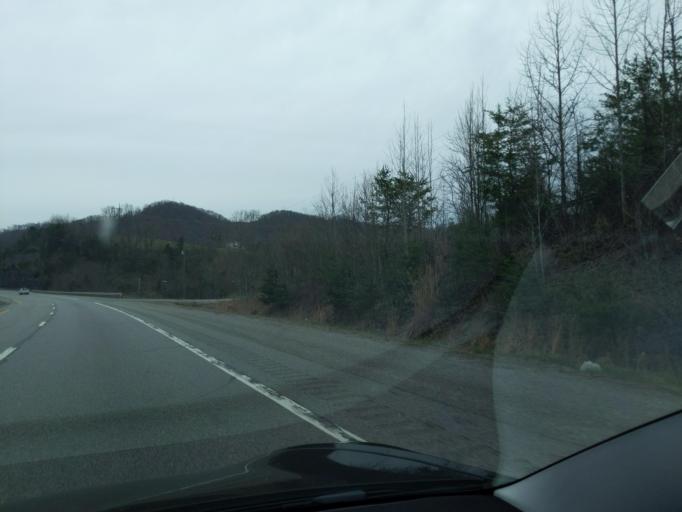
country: US
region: Kentucky
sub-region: Bell County
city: Pineville
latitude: 36.8204
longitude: -83.7725
